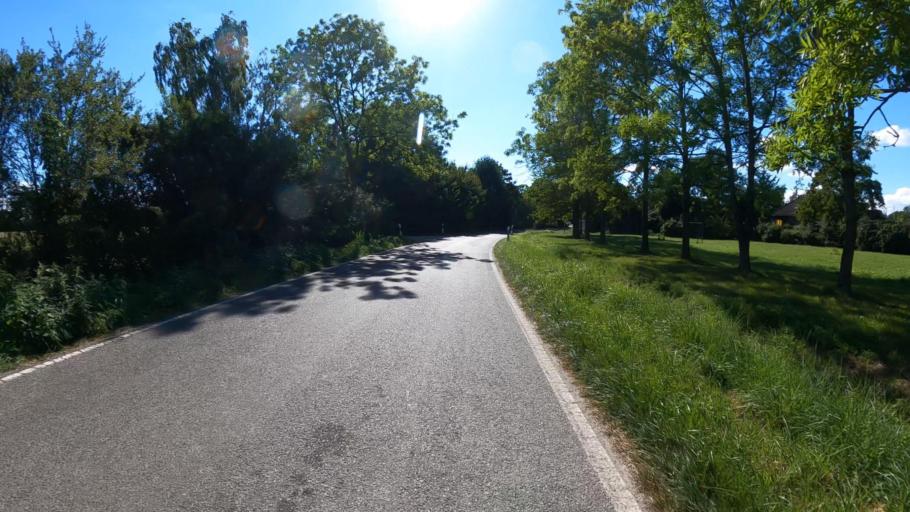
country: DE
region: Schleswig-Holstein
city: Schurensohlen
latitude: 53.7645
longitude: 10.5013
